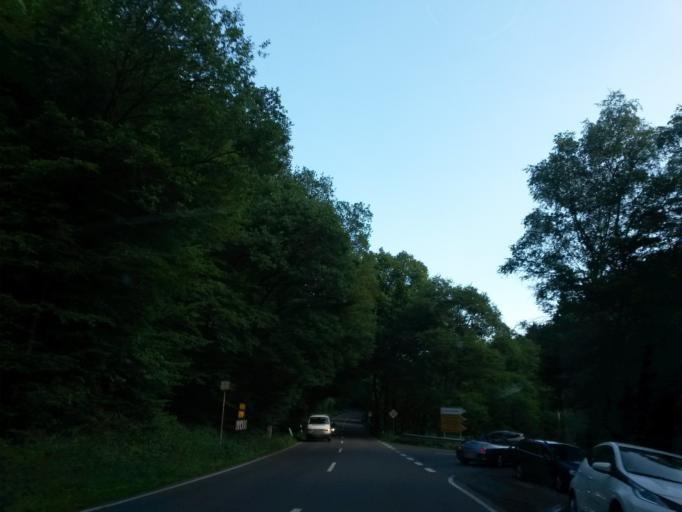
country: DE
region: North Rhine-Westphalia
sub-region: Regierungsbezirk Koln
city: Overath
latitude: 50.9169
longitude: 7.3266
